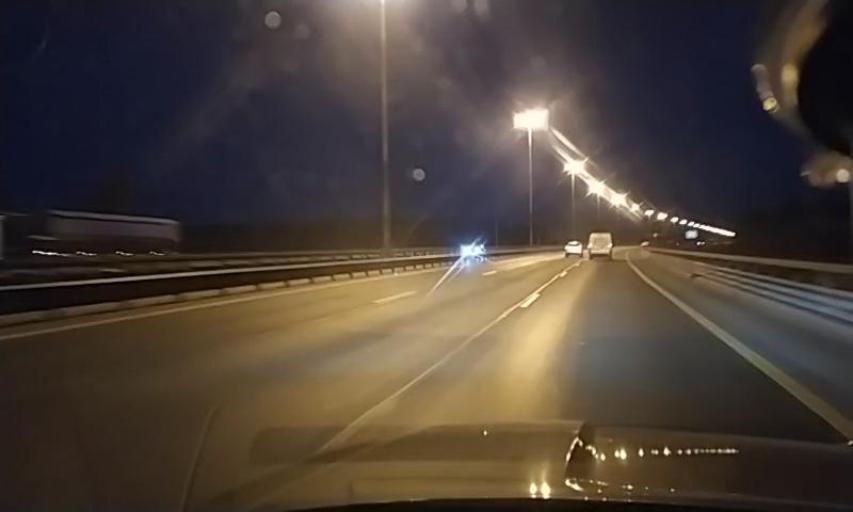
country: RU
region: St.-Petersburg
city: Pesochnyy
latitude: 60.0866
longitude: 30.1029
